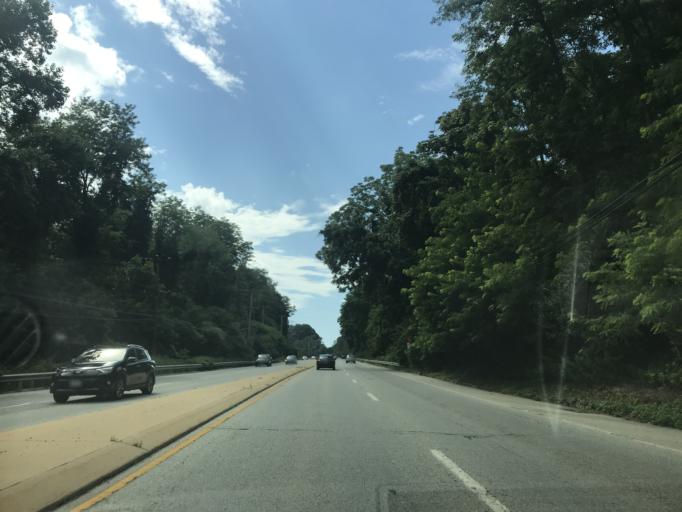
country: US
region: Pennsylvania
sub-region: Chester County
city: West Chester
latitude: 39.8724
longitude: -75.6091
